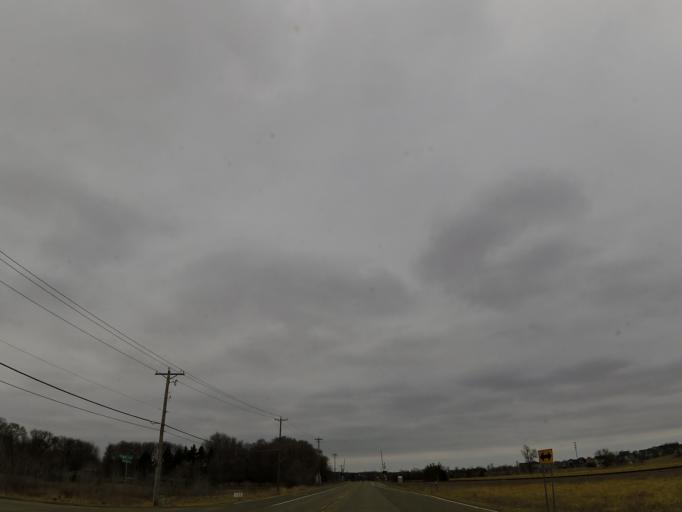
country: US
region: Minnesota
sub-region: Washington County
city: Bayport
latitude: 45.0068
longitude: -92.7942
